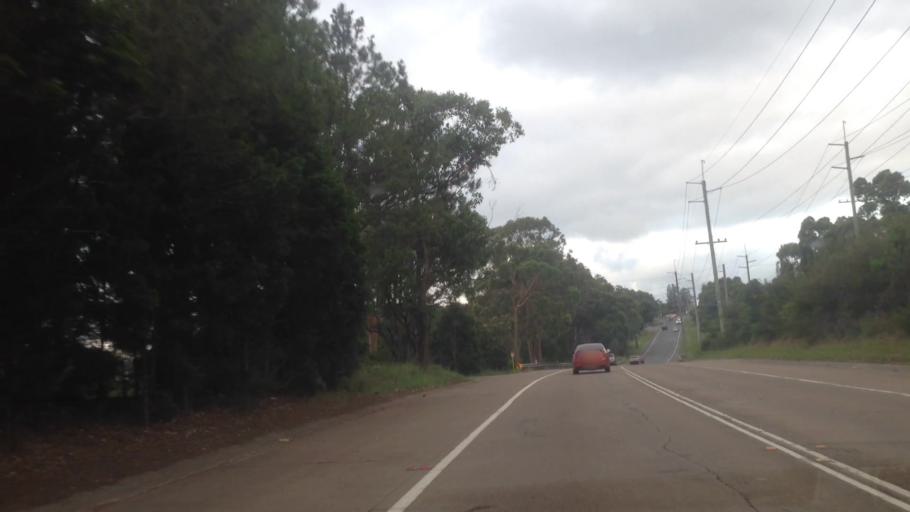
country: AU
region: New South Wales
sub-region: Lake Macquarie Shire
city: Dora Creek
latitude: -33.1148
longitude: 151.4723
